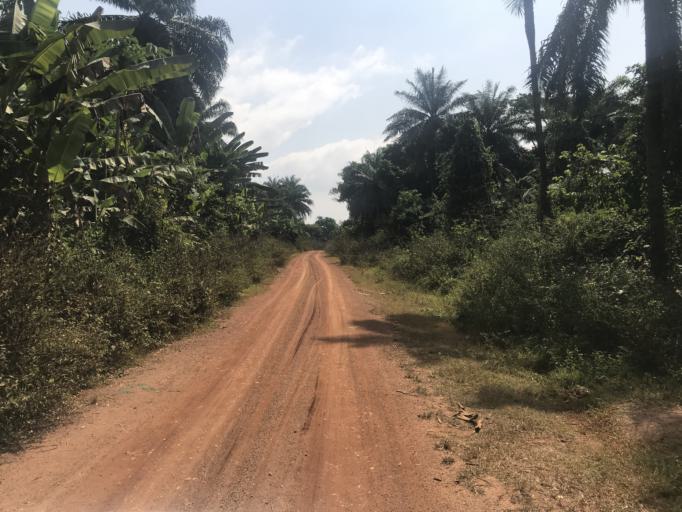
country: NG
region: Osun
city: Ikirun
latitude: 7.8347
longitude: 4.6320
